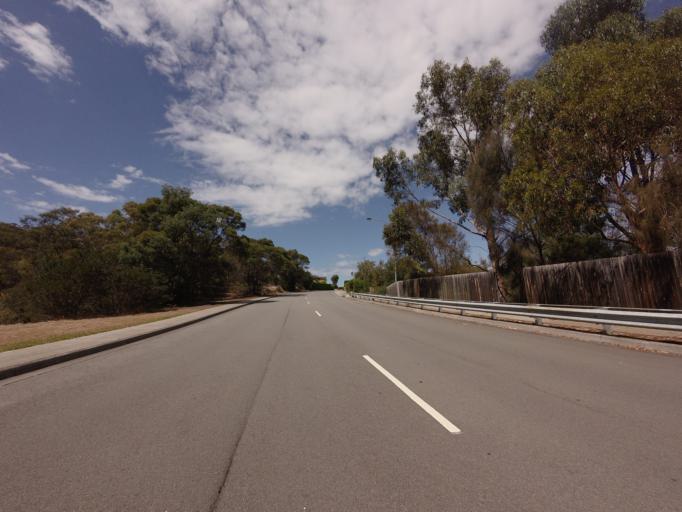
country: AU
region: Tasmania
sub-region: Clarence
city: Howrah
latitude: -42.8955
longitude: 147.4152
